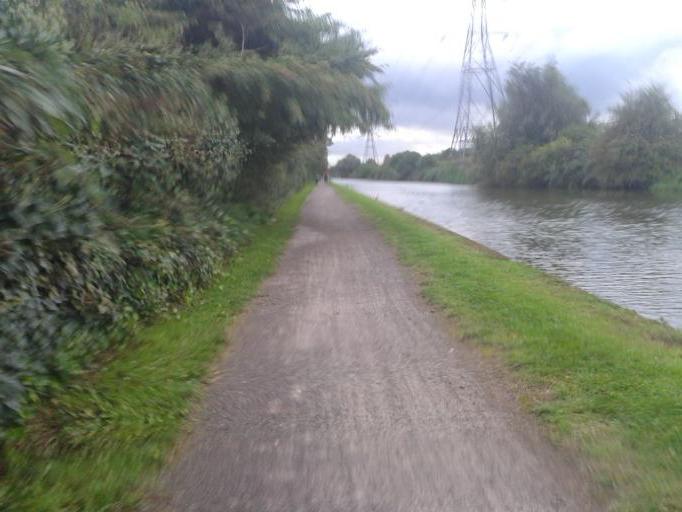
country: GB
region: England
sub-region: Greater London
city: Walthamstow
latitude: 51.6206
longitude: -0.0351
